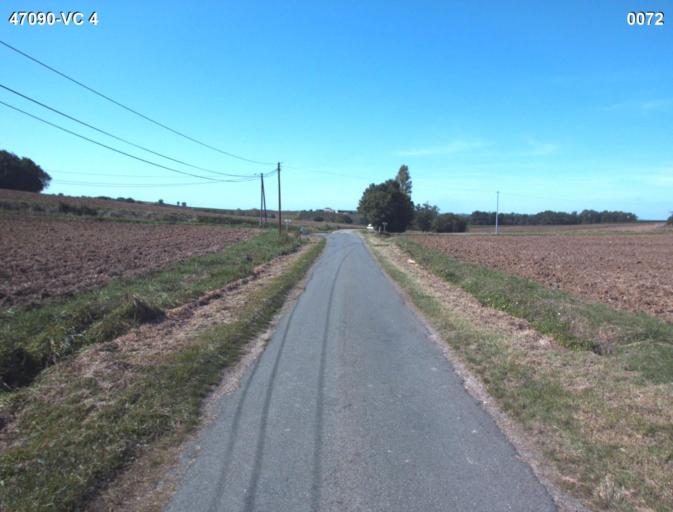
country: FR
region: Aquitaine
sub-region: Departement du Lot-et-Garonne
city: Vianne
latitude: 44.1783
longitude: 0.3440
